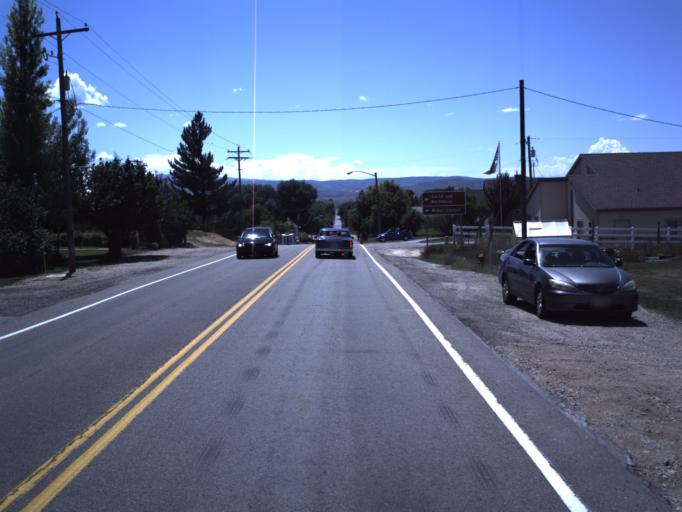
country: US
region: Utah
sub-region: Summit County
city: Oakley
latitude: 40.7176
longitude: -111.3003
